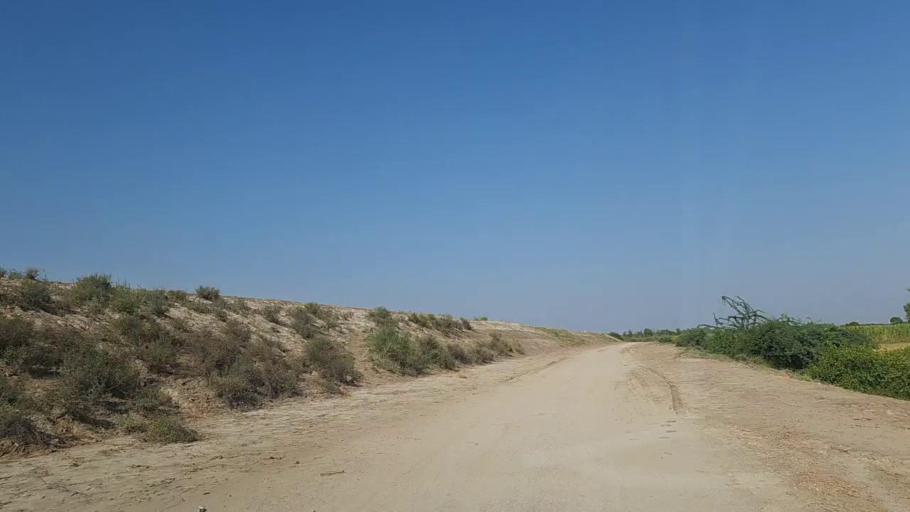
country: PK
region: Sindh
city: Chuhar Jamali
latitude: 24.5791
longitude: 68.0298
